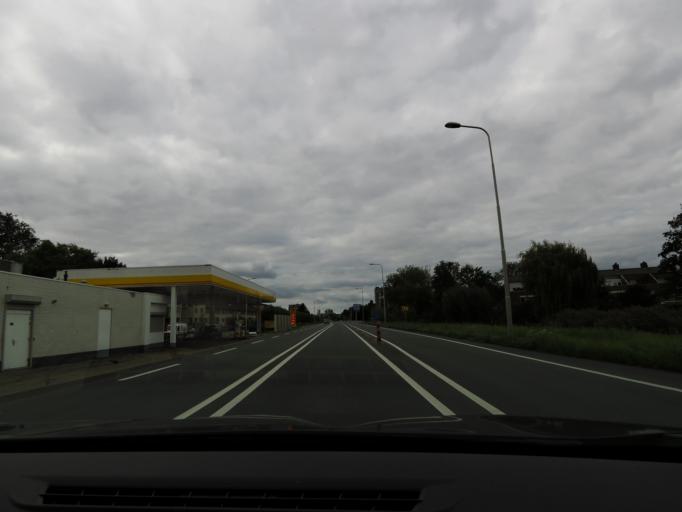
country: NL
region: South Holland
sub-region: Gemeente Krimpen aan den IJssel
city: Krimpen aan den IJssel
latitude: 51.9092
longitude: 4.5934
